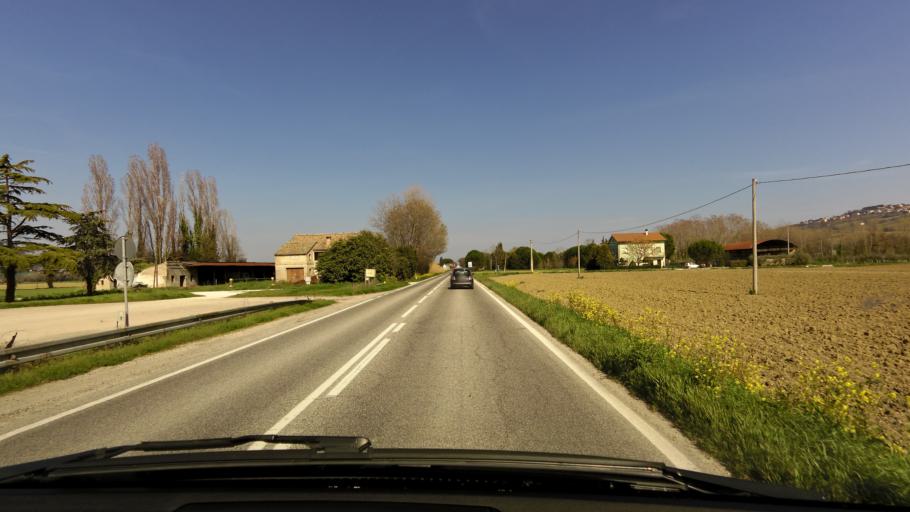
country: IT
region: The Marches
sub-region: Provincia di Macerata
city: Potenza Picena
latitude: 43.3759
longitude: 13.5981
